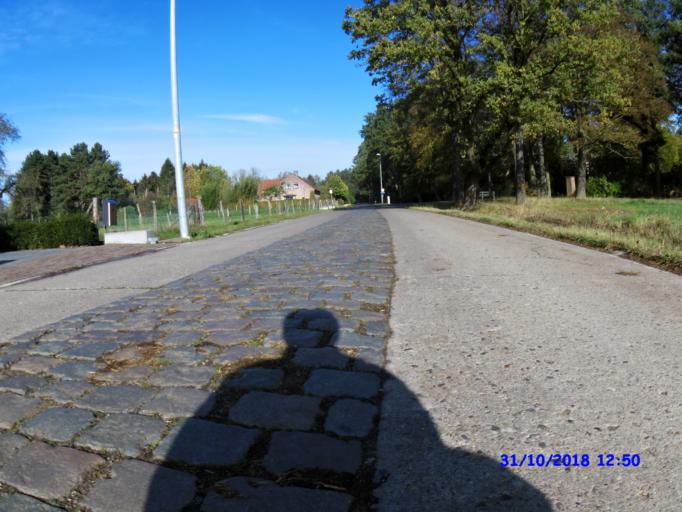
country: BE
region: Flanders
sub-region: Provincie Antwerpen
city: Turnhout
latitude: 51.2875
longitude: 4.9599
